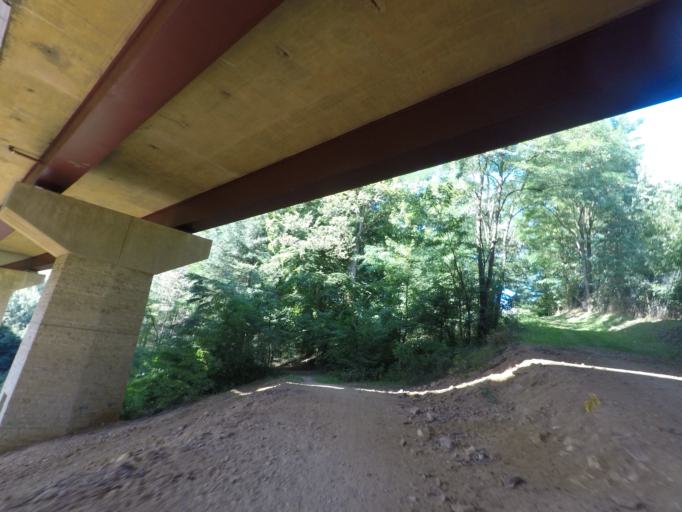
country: LU
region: Luxembourg
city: Itzig
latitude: 49.6080
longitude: 6.1740
